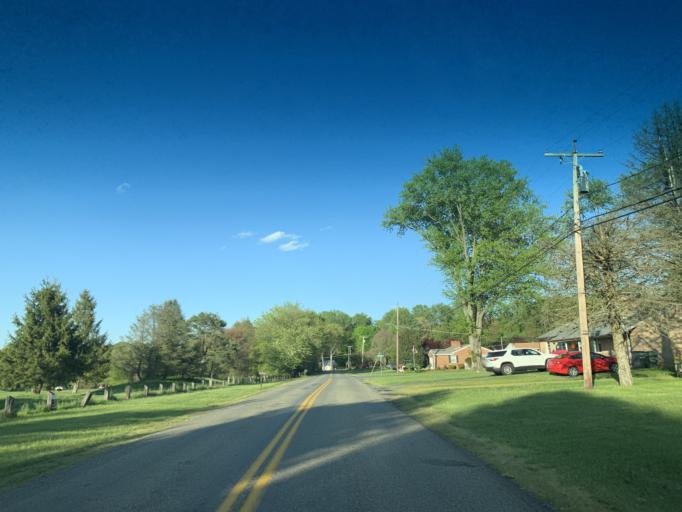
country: US
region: Maryland
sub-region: Harford County
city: Aberdeen
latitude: 39.5402
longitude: -76.1817
